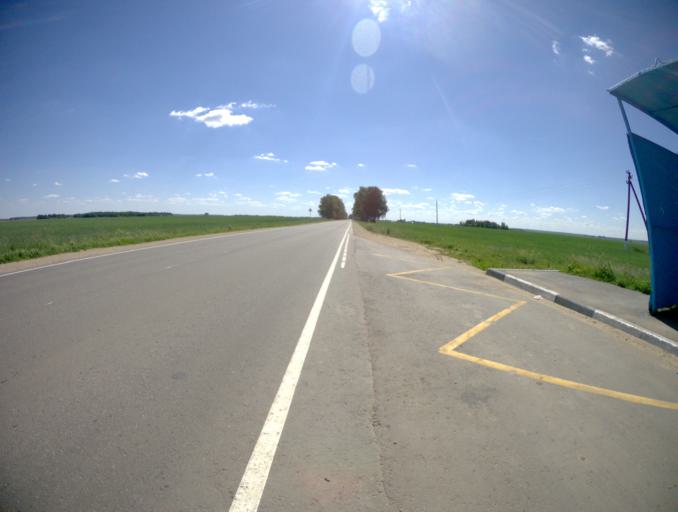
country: RU
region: Ivanovo
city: Gavrilov Posad
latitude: 56.5308
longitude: 40.2297
